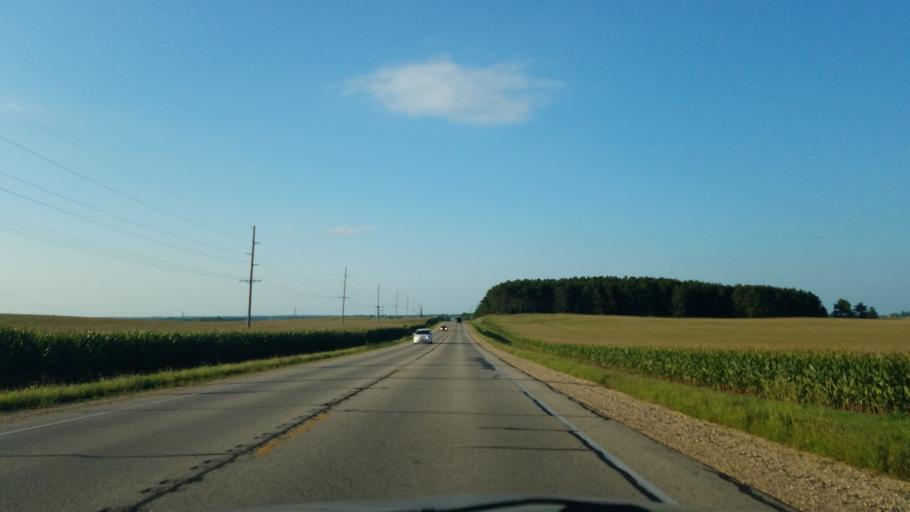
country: US
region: Wisconsin
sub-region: Saint Croix County
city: Roberts
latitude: 45.0294
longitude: -92.5375
